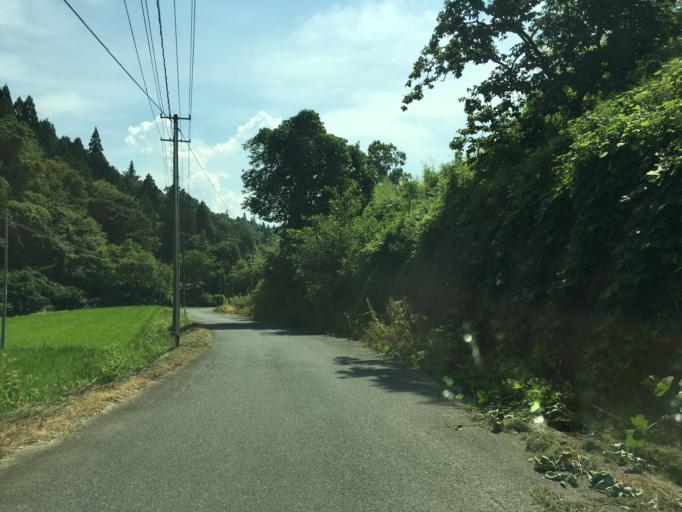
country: JP
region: Fukushima
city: Ishikawa
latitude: 37.1935
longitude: 140.4715
